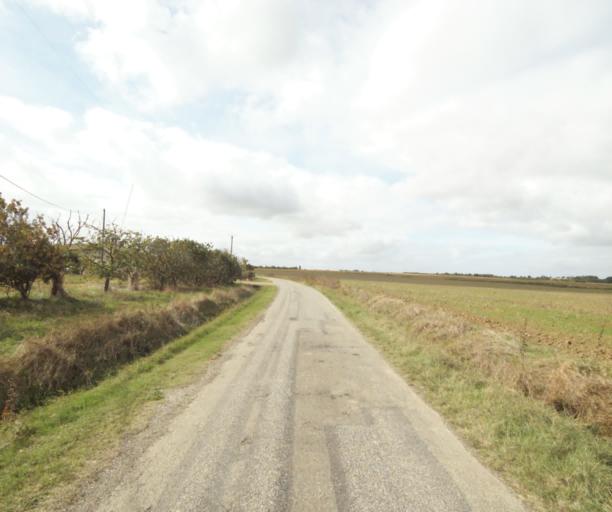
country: FR
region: Midi-Pyrenees
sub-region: Departement du Tarn-et-Garonne
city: Finhan
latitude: 43.8875
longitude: 1.1319
